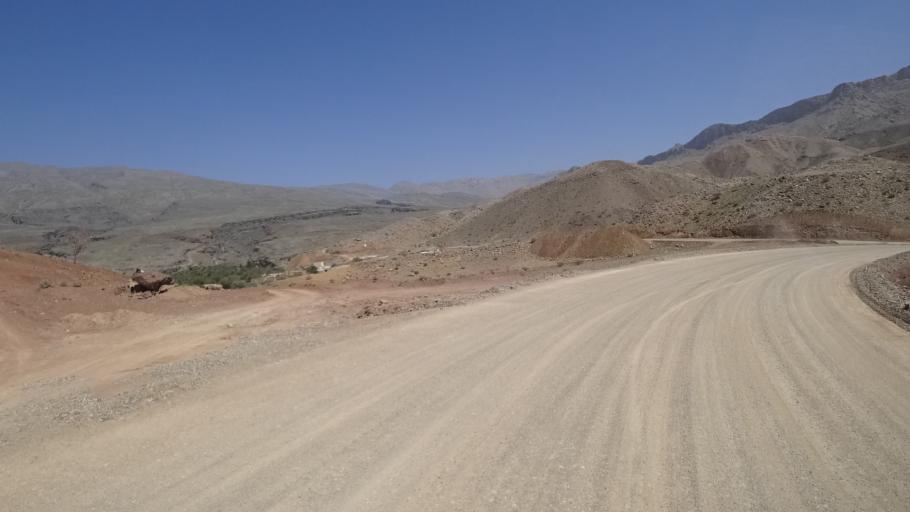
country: OM
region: Muhafazat ad Dakhiliyah
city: Bahla'
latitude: 23.2257
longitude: 57.0639
